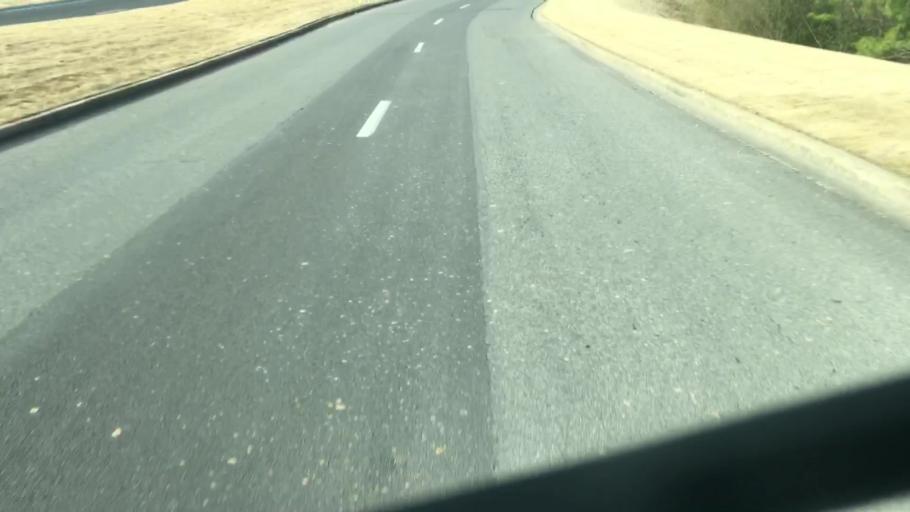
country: US
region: Alabama
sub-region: Jefferson County
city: Cahaba Heights
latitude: 33.4772
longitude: -86.7036
